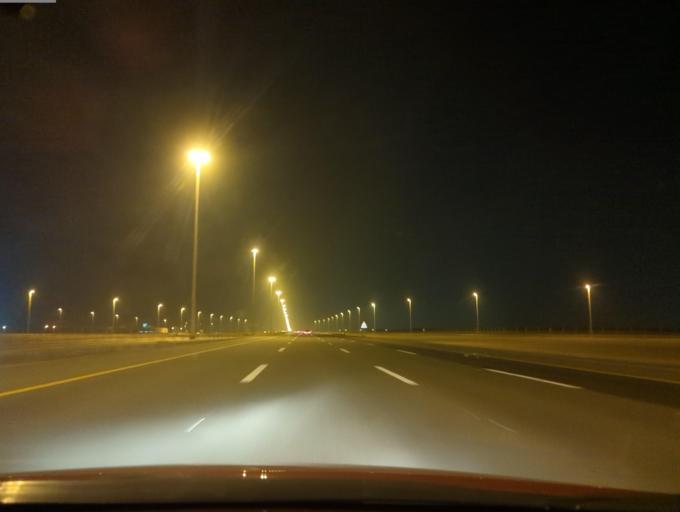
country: AE
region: Abu Dhabi
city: Abu Dhabi
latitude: 24.5538
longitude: 54.7465
